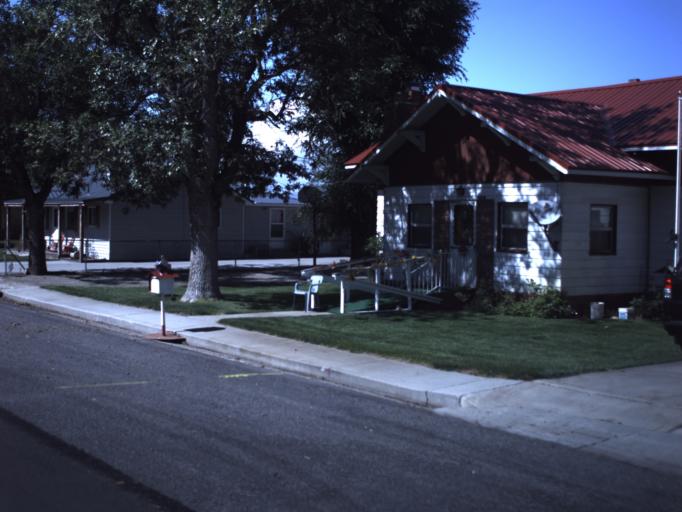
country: US
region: Utah
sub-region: Utah County
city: Benjamin
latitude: 40.0981
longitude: -111.7324
